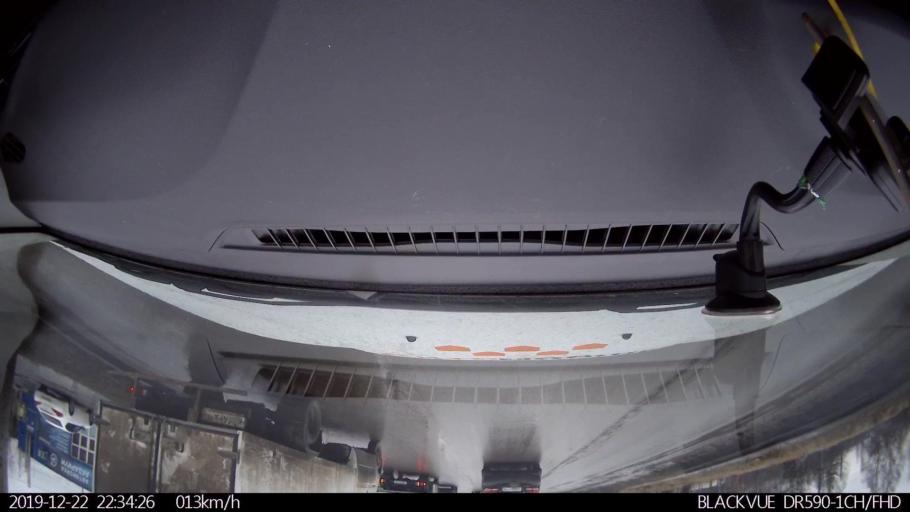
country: RU
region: Nizjnij Novgorod
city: Gorbatovka
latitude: 56.3142
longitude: 43.8680
